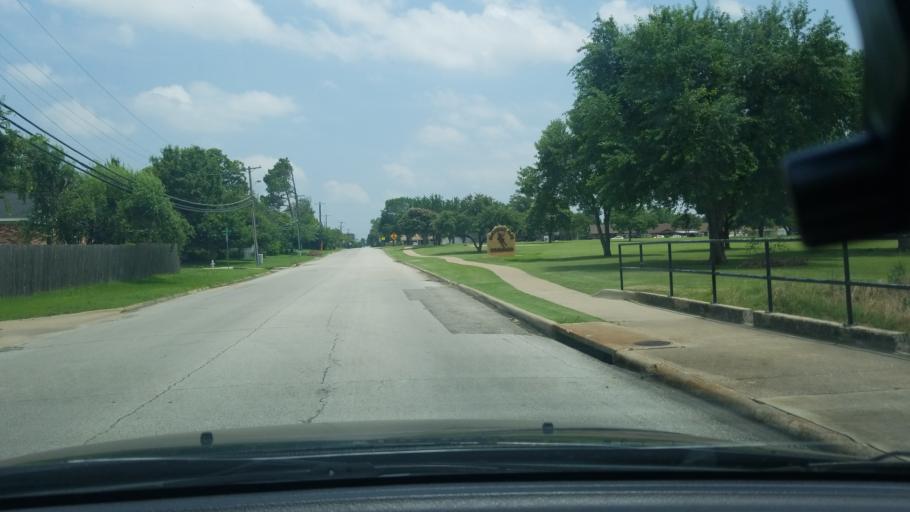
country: US
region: Texas
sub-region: Dallas County
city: Mesquite
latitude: 32.7986
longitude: -96.6446
